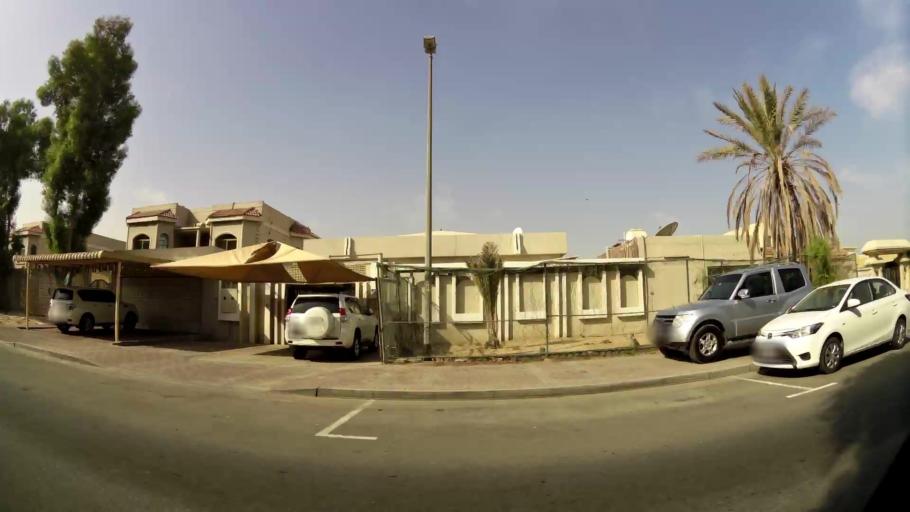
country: AE
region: Ash Shariqah
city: Sharjah
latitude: 25.2186
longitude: 55.3894
